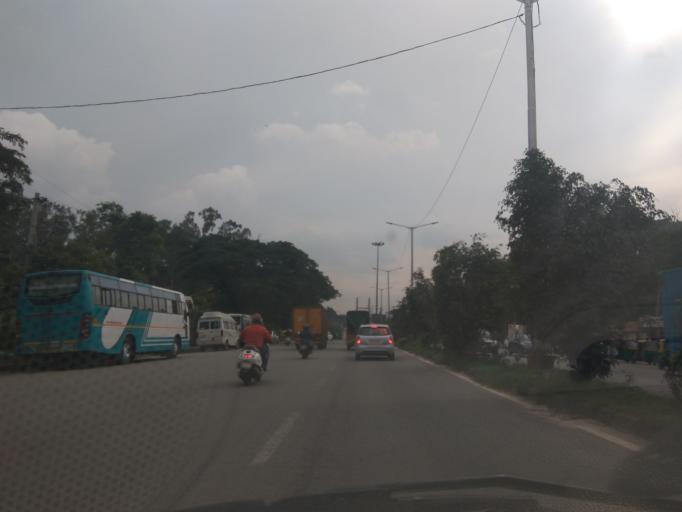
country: IN
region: Karnataka
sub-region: Bangalore Urban
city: Bangalore
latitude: 13.0056
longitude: 77.6860
